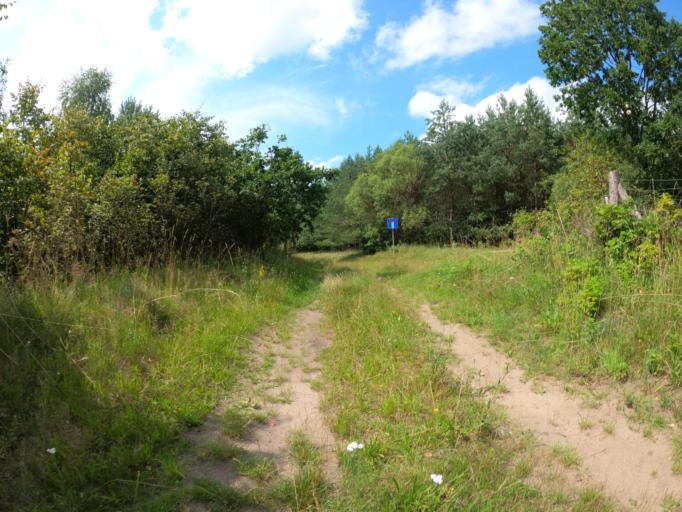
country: PL
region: West Pomeranian Voivodeship
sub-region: Powiat szczecinecki
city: Grzmiaca
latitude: 53.8291
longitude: 16.4578
